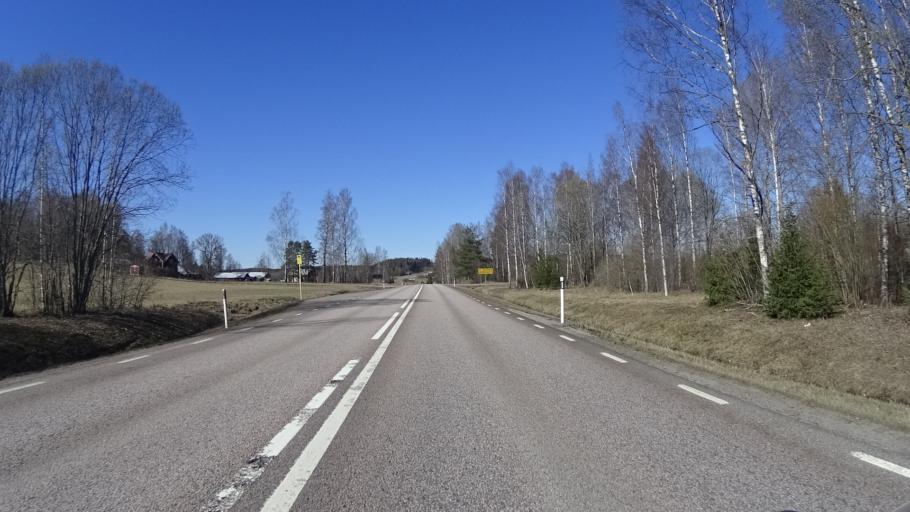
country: SE
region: Vaermland
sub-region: Karlstads Kommun
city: Edsvalla
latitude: 59.5724
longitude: 13.0213
